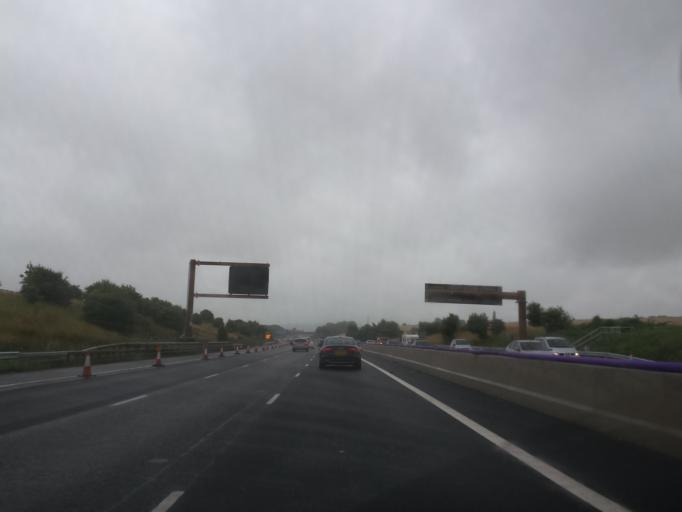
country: GB
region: England
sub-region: Derbyshire
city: Bolsover
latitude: 53.2239
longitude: -1.3303
